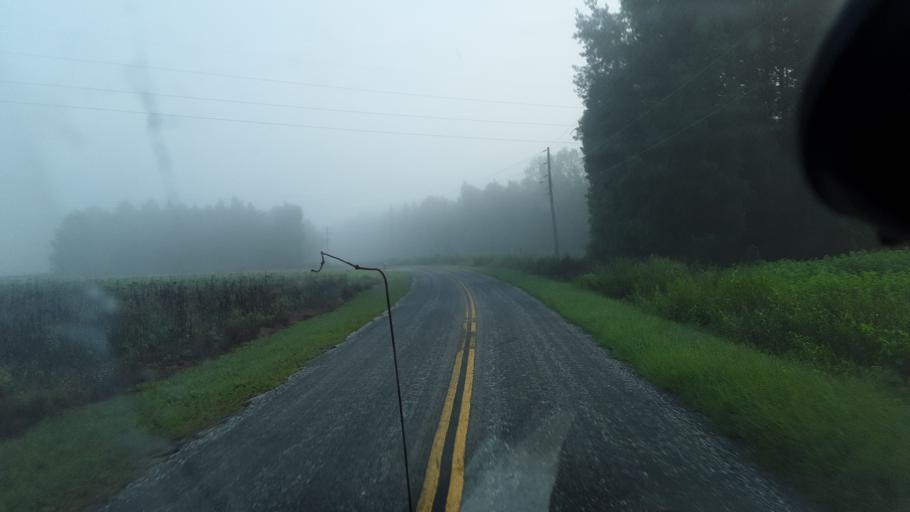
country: US
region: South Carolina
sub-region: Williamsburg County
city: Kingstree
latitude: 33.8121
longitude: -79.9626
